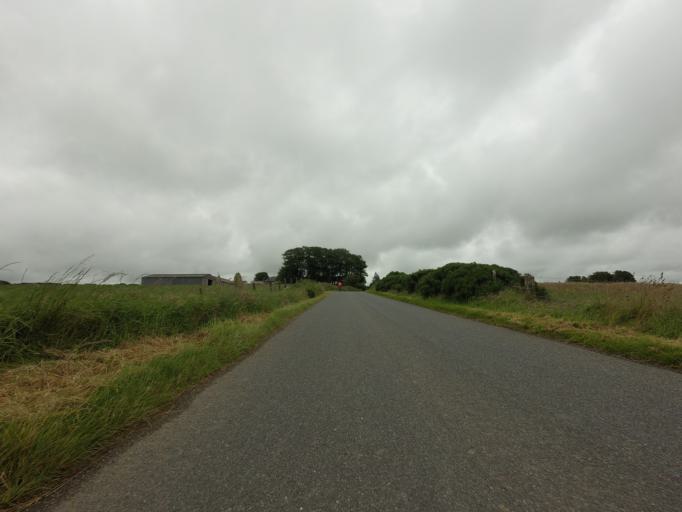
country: GB
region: Scotland
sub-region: Aberdeenshire
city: Turriff
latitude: 57.5430
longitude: -2.2637
